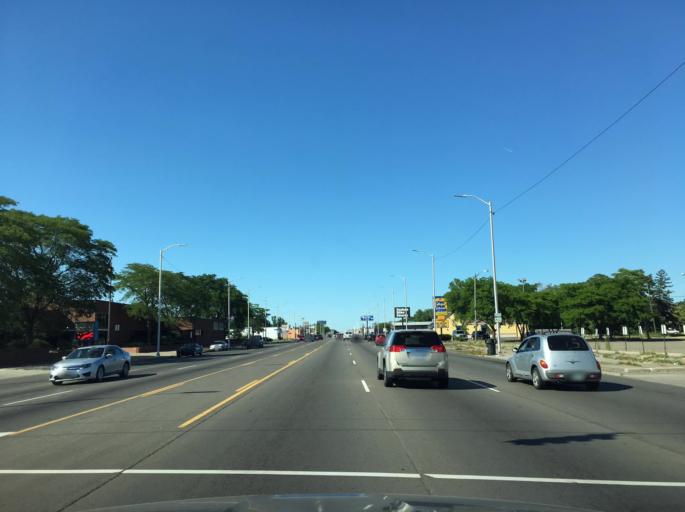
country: US
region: Michigan
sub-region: Wayne County
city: Hamtramck
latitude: 42.4085
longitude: -82.9951
